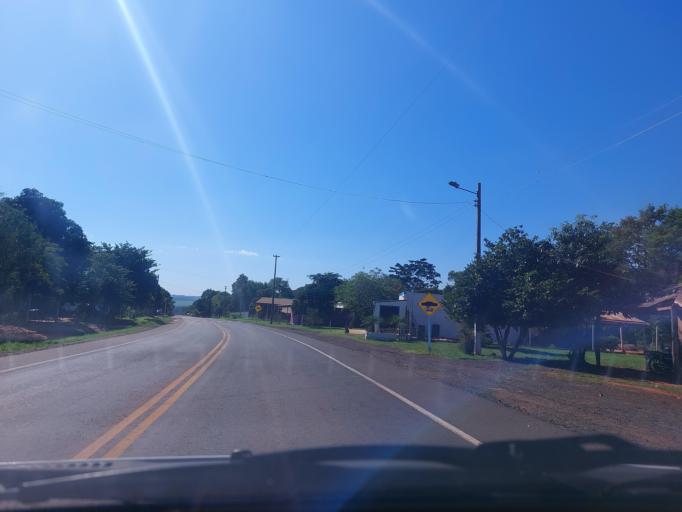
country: PY
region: San Pedro
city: Guayaybi
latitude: -24.3153
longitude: -56.1610
